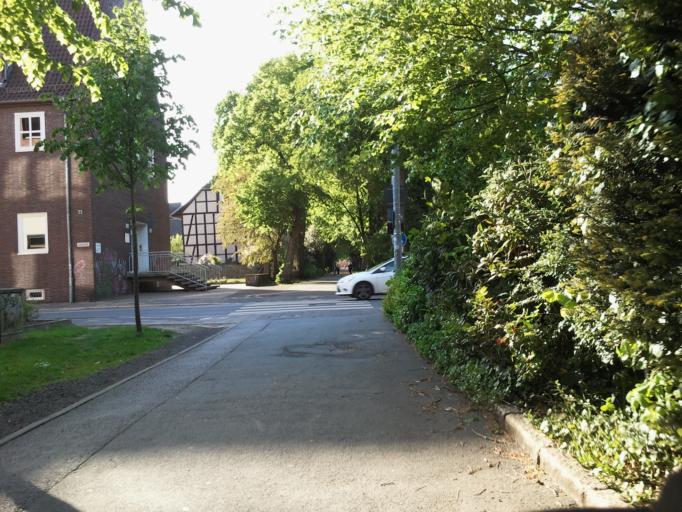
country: DE
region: Lower Saxony
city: Nienburg
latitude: 52.6399
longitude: 9.2107
